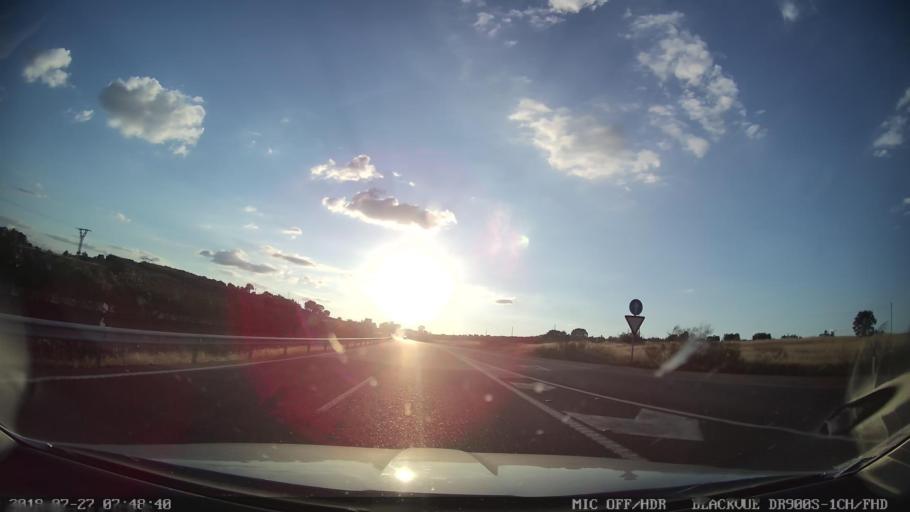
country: ES
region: Extremadura
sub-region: Provincia de Badajoz
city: San Pedro de Merida
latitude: 38.9476
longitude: -6.1902
